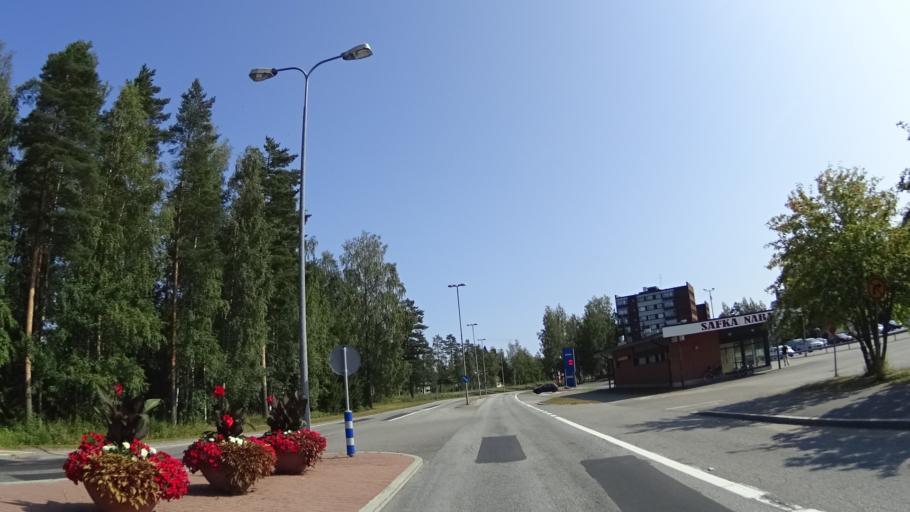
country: FI
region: Pirkanmaa
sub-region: Ylae-Pirkanmaa
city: Maenttae
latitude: 62.0295
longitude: 24.6149
